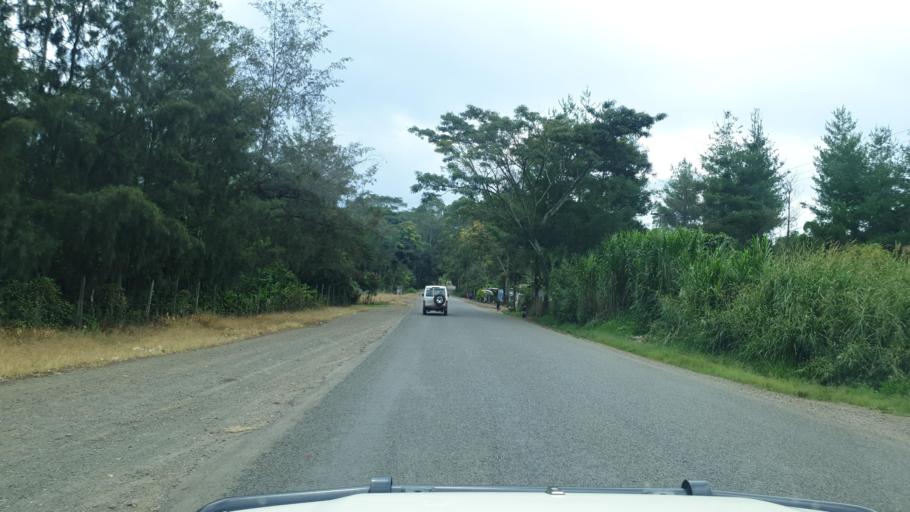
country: PG
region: Eastern Highlands
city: Goroka
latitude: -6.0454
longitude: 145.3762
